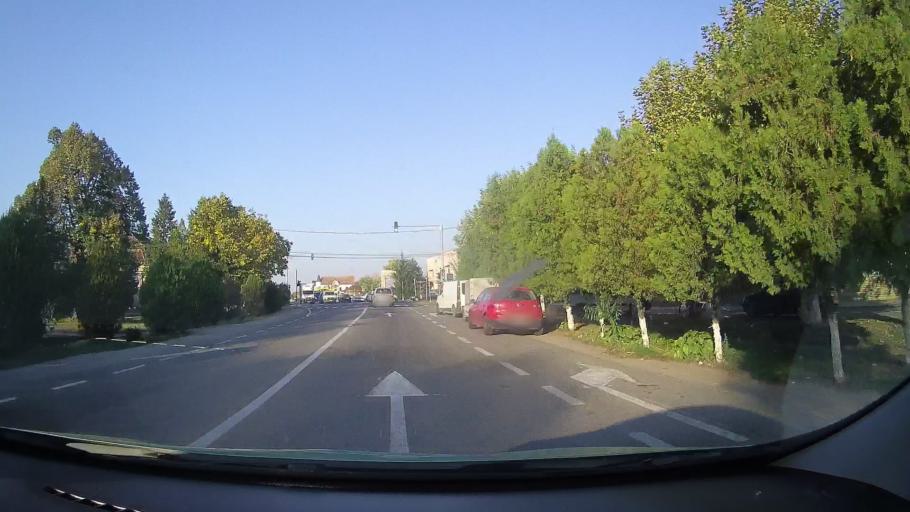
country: RO
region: Arad
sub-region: Comuna Pancota
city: Pancota
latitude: 46.3232
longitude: 21.6880
